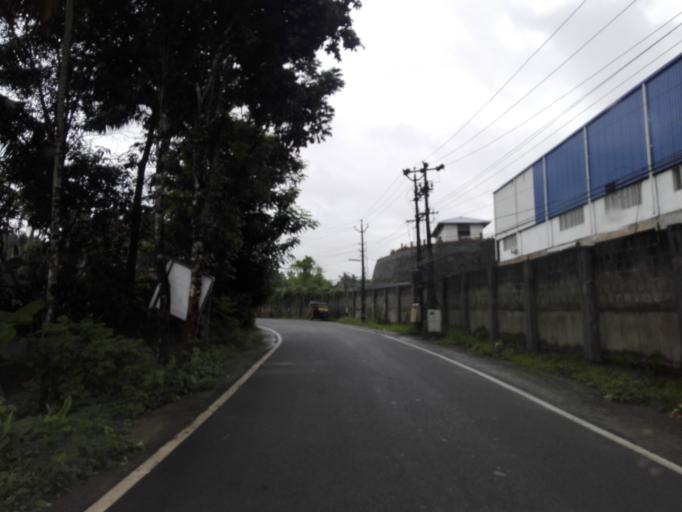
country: IN
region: Kerala
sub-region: Ernakulam
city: Aluva
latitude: 10.0562
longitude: 76.3617
